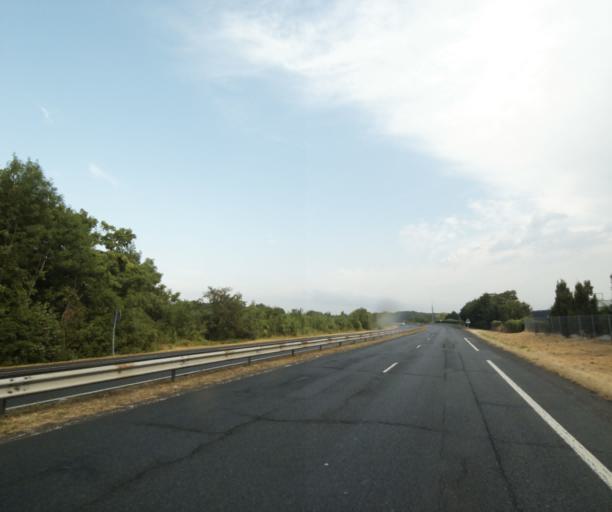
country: FR
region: Ile-de-France
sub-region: Departement du Val-d'Oise
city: Neuville-sur-Oise
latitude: 49.0043
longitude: 2.0754
